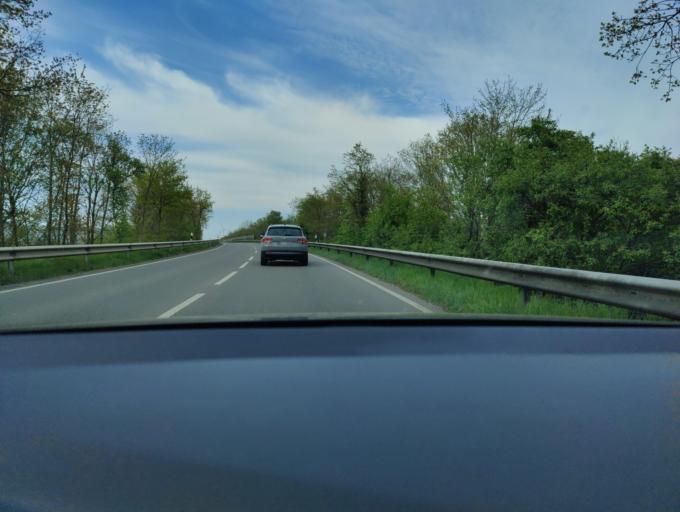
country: NL
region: Overijssel
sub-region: Gemeente Losser
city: Losser
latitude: 52.3080
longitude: 7.0618
